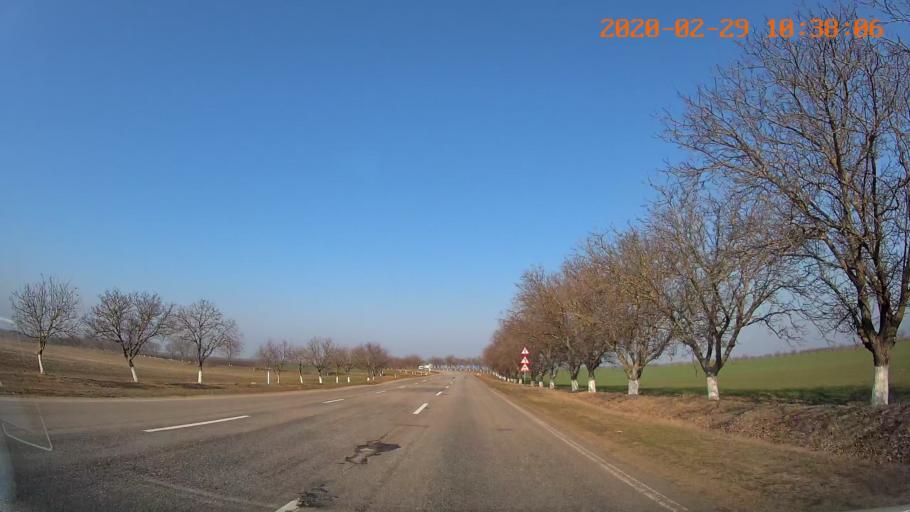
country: MD
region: Anenii Noi
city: Varnita
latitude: 47.0132
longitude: 29.4790
